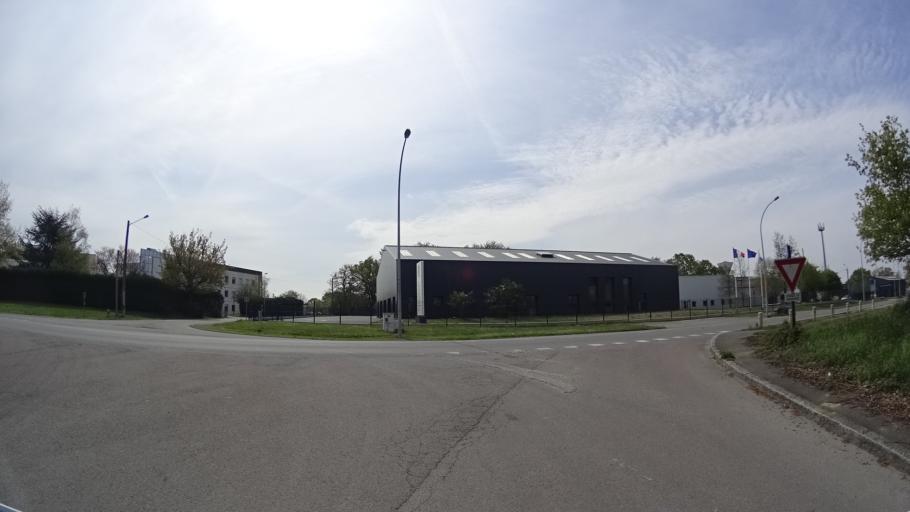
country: FR
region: Brittany
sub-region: Departement d'Ille-et-Vilaine
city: Chartres-de-Bretagne
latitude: 48.0348
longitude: -1.7257
